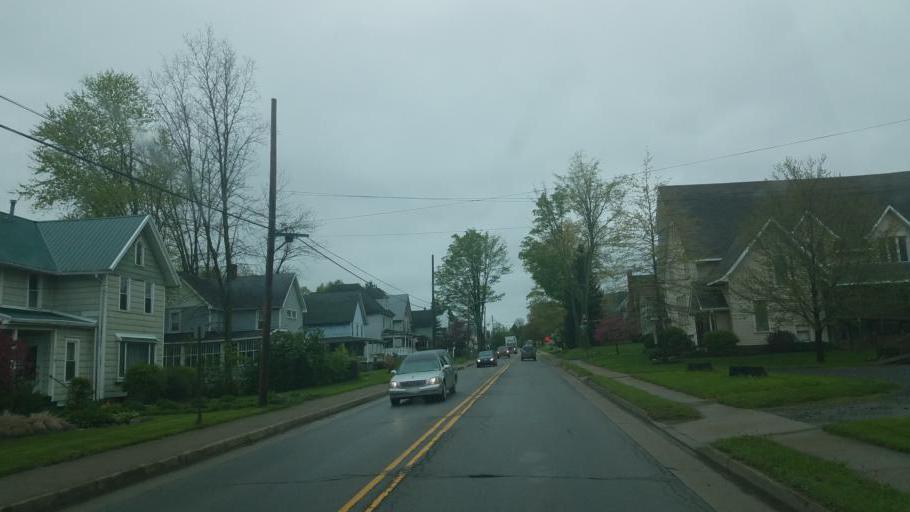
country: US
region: Pennsylvania
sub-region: McKean County
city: Port Allegany
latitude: 41.8159
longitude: -78.2840
